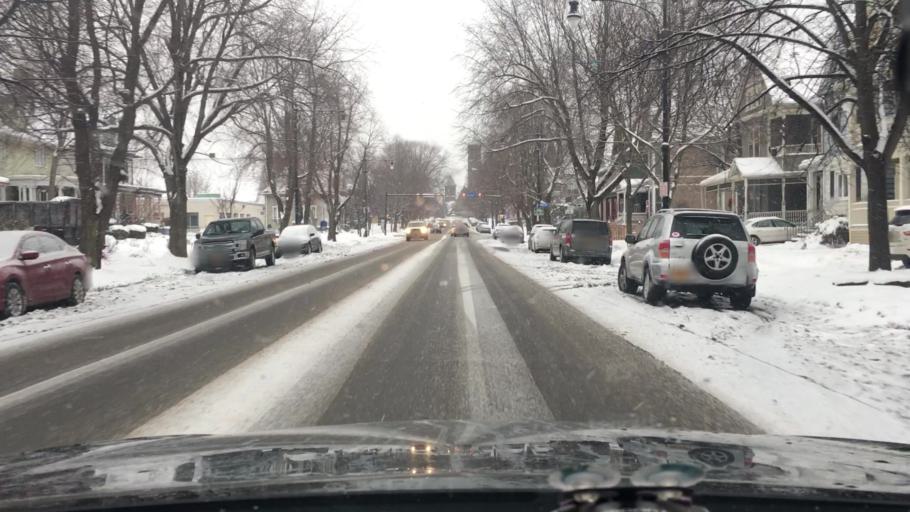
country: US
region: New York
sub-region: Erie County
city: Buffalo
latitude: 42.9060
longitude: -78.8820
